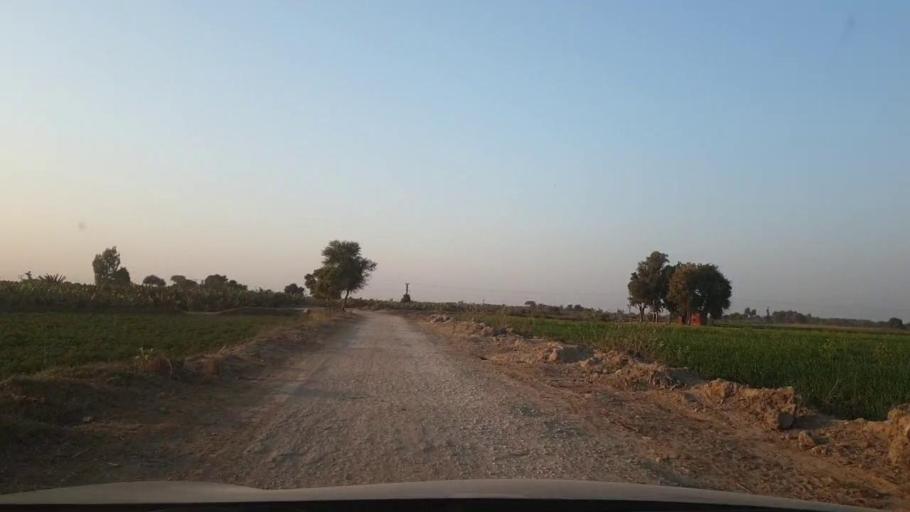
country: PK
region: Sindh
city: Tando Allahyar
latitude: 25.4986
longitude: 68.7405
